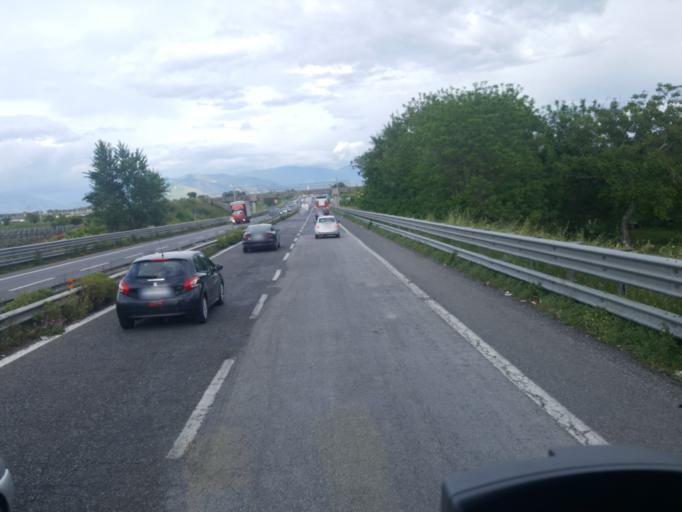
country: IT
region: Campania
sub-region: Provincia di Napoli
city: Pascarola
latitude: 40.9734
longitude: 14.3148
